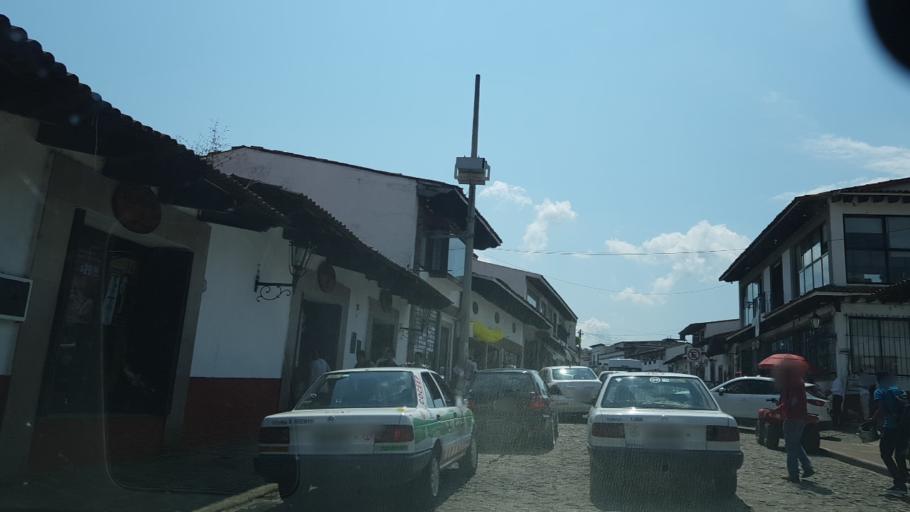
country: MX
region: Mexico
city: Valle de Bravo
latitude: 19.1968
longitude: -100.1319
